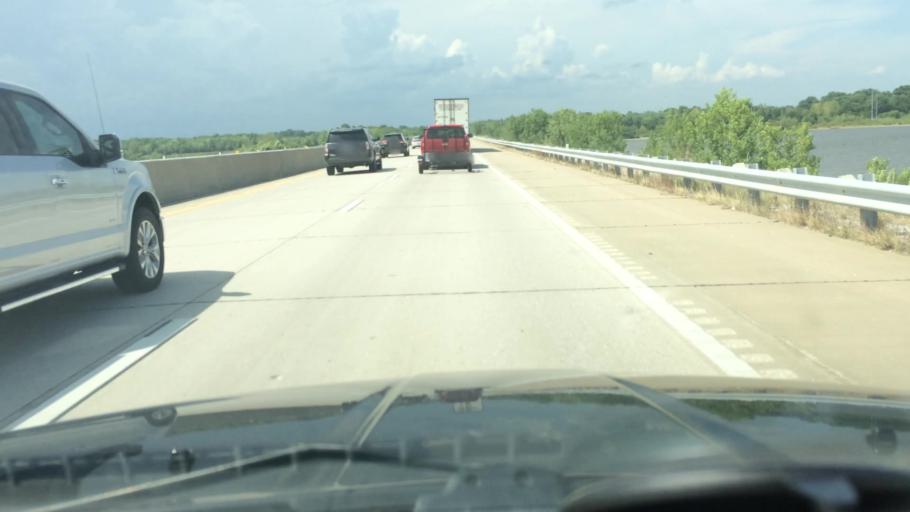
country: US
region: Missouri
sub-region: Henry County
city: Clinton
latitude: 38.3226
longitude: -93.7570
